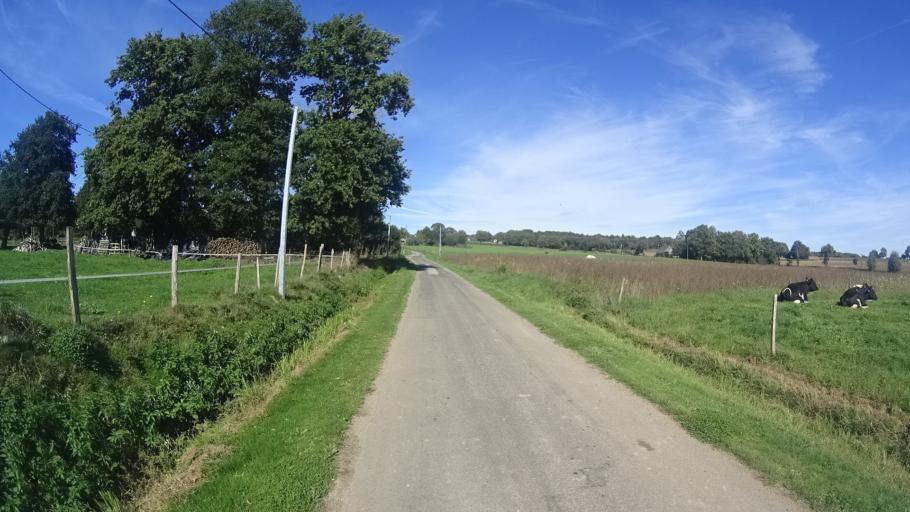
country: FR
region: Brittany
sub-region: Departement du Morbihan
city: Peillac
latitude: 47.7331
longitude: -2.1817
